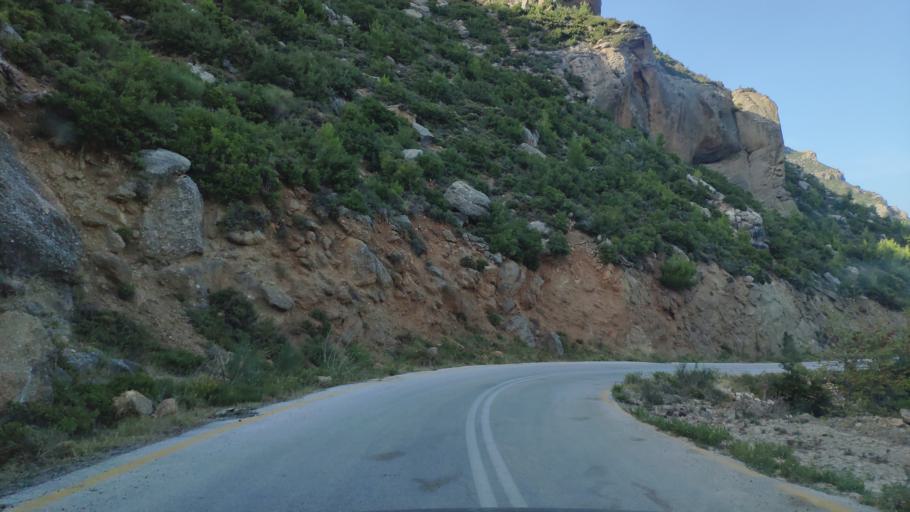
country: GR
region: West Greece
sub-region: Nomos Achaias
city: Aiyira
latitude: 38.0636
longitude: 22.3779
